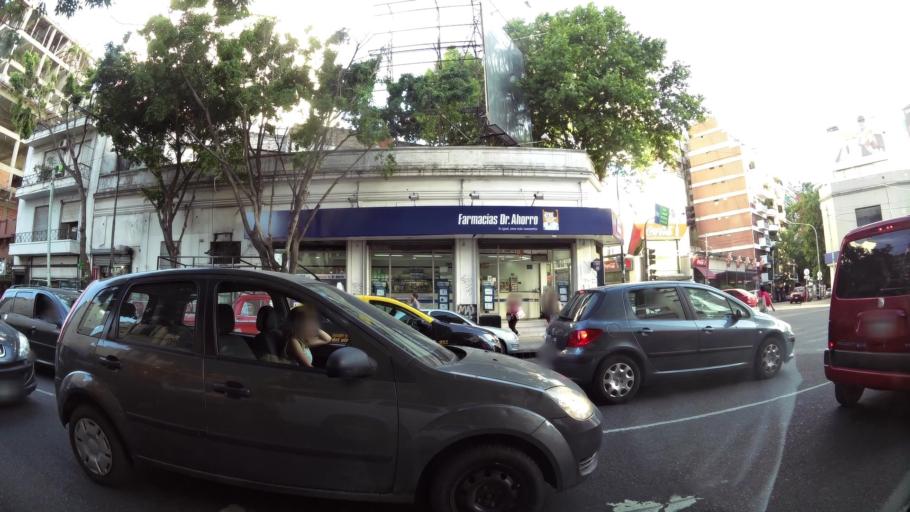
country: AR
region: Buenos Aires F.D.
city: Colegiales
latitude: -34.6017
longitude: -58.4321
